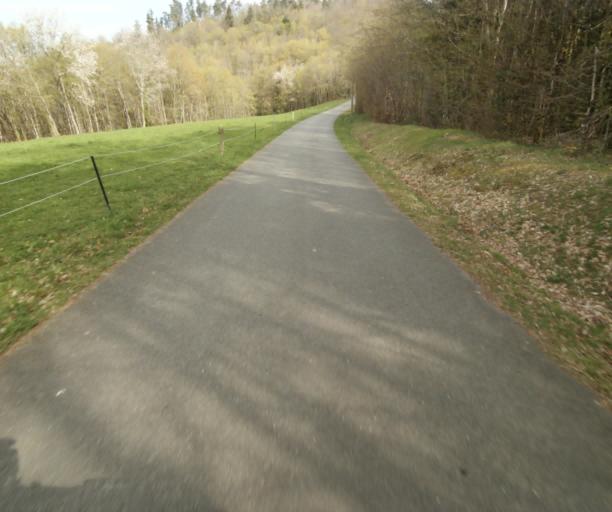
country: FR
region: Limousin
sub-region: Departement de la Correze
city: Correze
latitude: 45.3627
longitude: 1.8160
